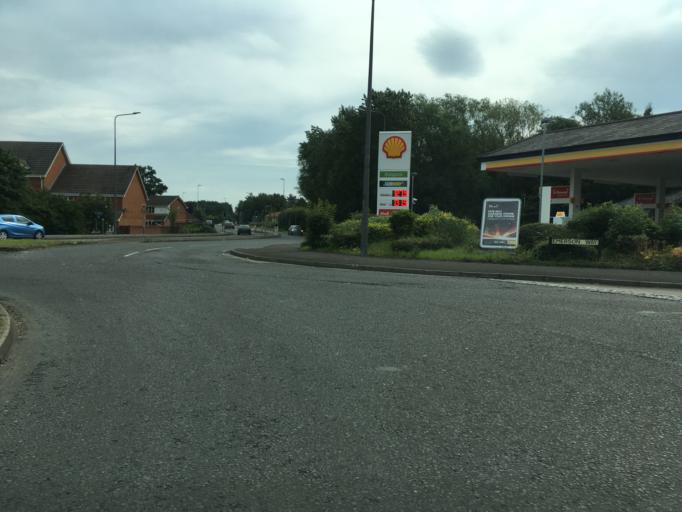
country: GB
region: England
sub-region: South Gloucestershire
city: Mangotsfield
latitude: 51.4968
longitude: -2.4831
